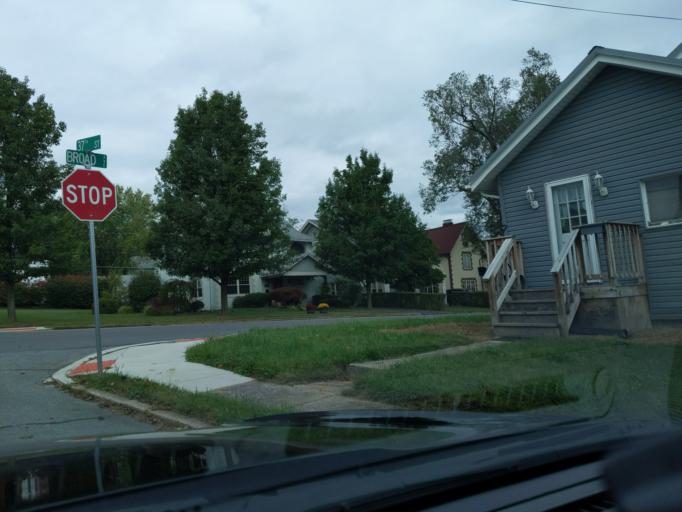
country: US
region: Pennsylvania
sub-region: Blair County
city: Lakemont
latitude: 40.4904
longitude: -78.4193
